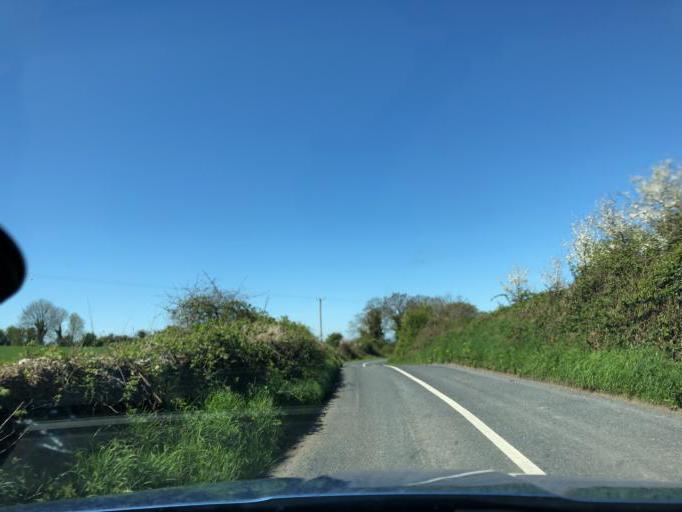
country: IE
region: Connaught
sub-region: County Galway
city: Loughrea
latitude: 53.1582
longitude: -8.3921
